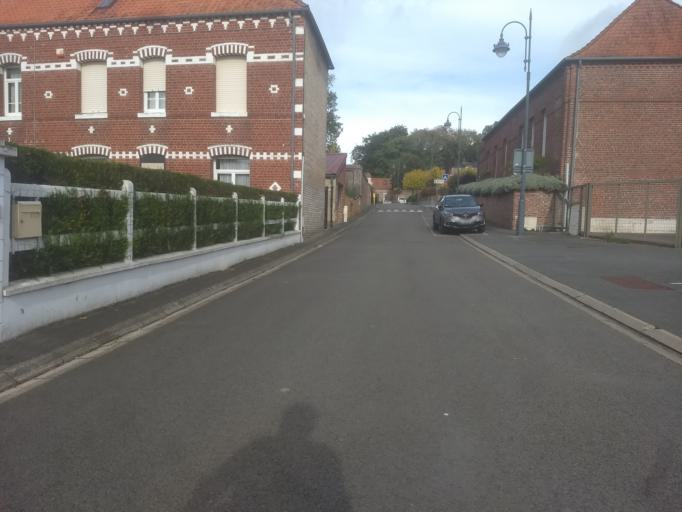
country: FR
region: Nord-Pas-de-Calais
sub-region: Departement du Pas-de-Calais
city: Dainville
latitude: 50.2803
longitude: 2.7227
